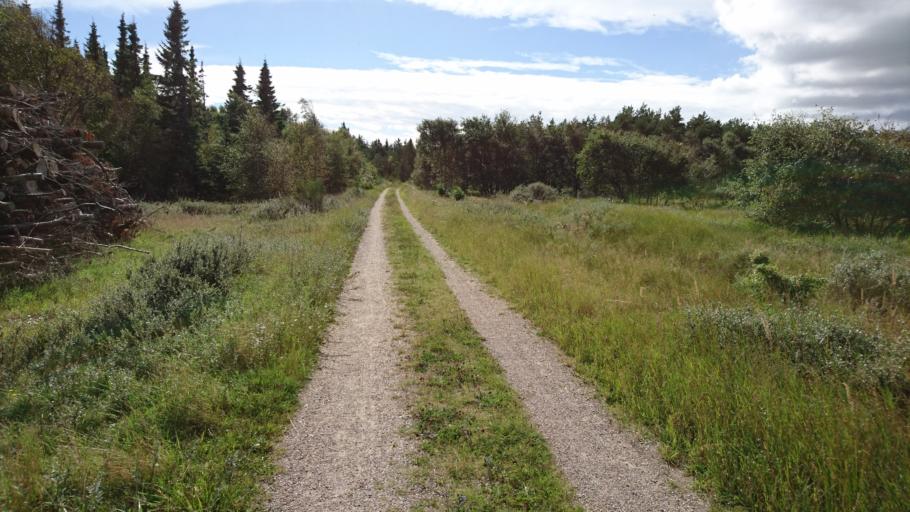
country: DK
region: North Denmark
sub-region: Frederikshavn Kommune
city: Skagen
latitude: 57.7128
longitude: 10.5138
